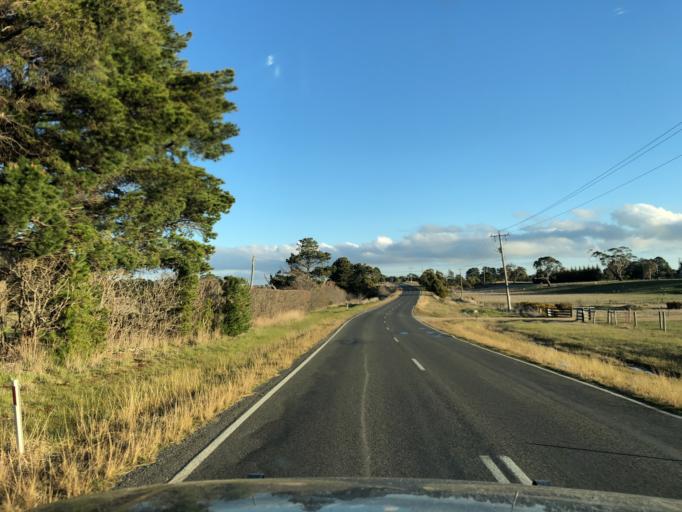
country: AU
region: Victoria
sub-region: Moorabool
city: Bacchus Marsh
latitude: -37.5860
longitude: 144.2367
